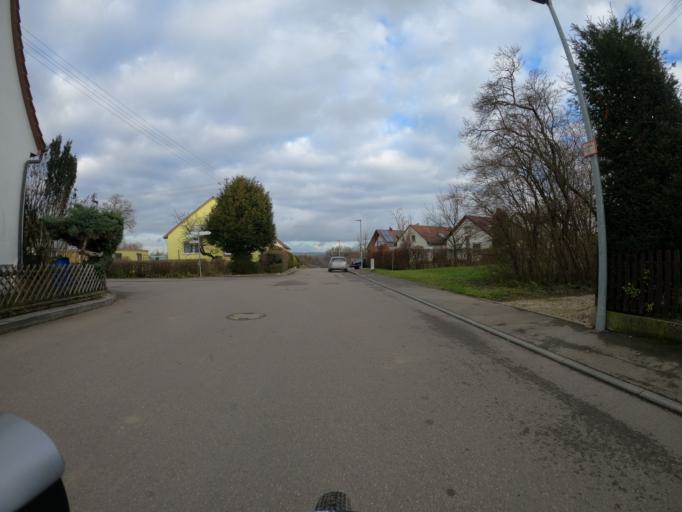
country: DE
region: Baden-Wuerttemberg
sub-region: Regierungsbezirk Stuttgart
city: Notzingen
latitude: 48.6748
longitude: 9.4733
